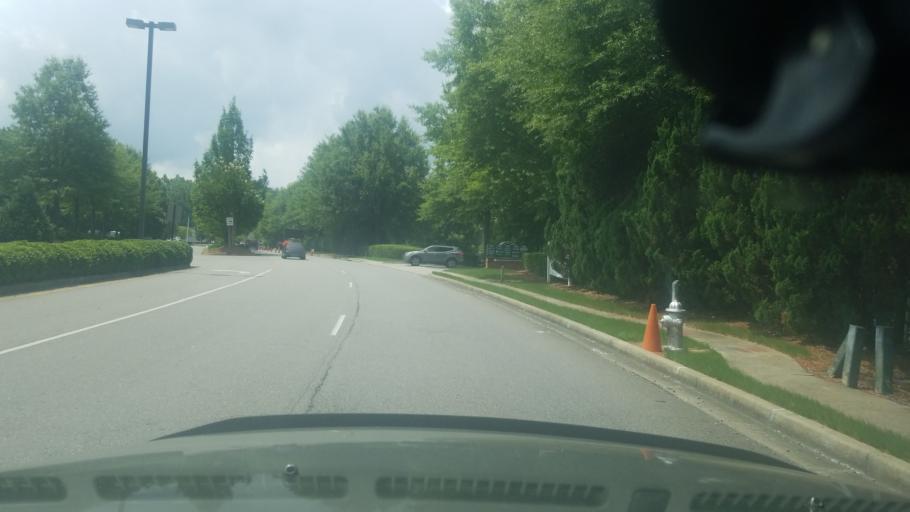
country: US
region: Georgia
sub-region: Fulton County
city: Johns Creek
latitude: 34.0713
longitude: -84.1725
